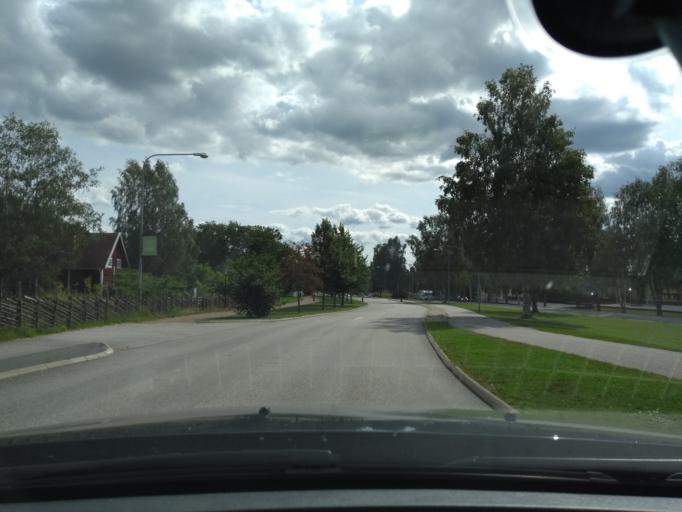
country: SE
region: Kalmar
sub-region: Vimmerby Kommun
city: Vimmerby
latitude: 57.6761
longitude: 15.8547
